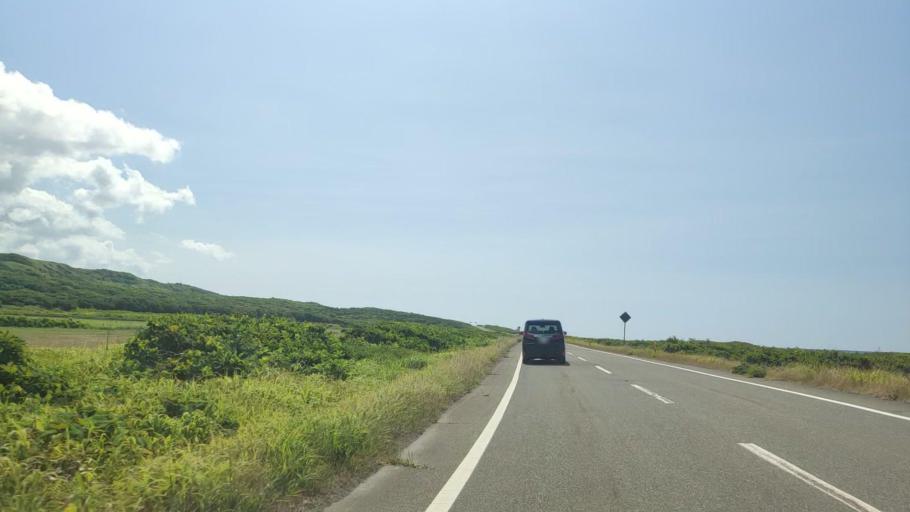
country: JP
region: Hokkaido
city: Wakkanai
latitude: 45.2366
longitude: 141.5764
